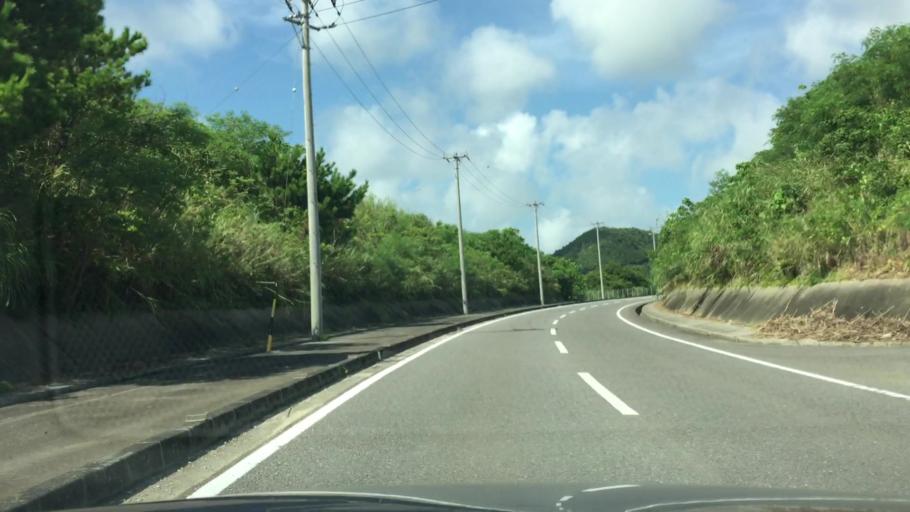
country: JP
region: Okinawa
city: Ishigaki
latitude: 24.4115
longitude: 124.2293
